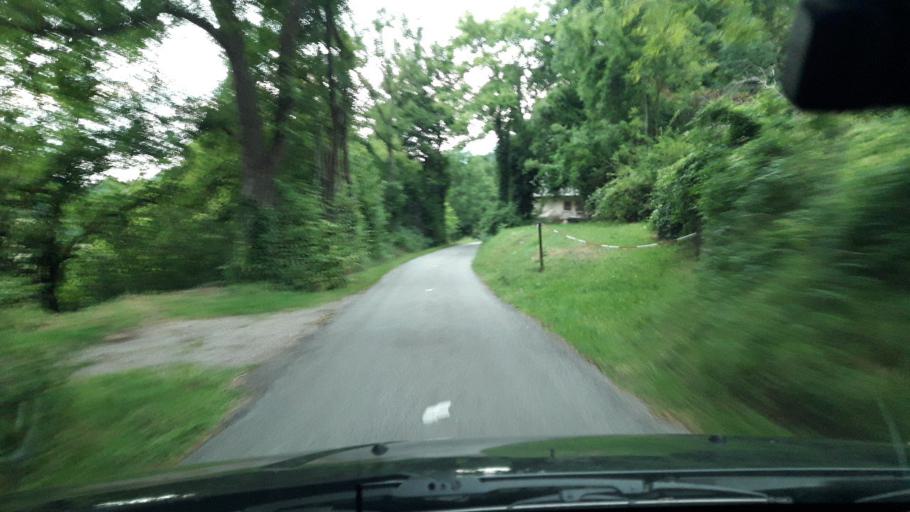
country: FR
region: Rhone-Alpes
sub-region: Departement de la Savoie
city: Barberaz
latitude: 45.5291
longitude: 5.9270
